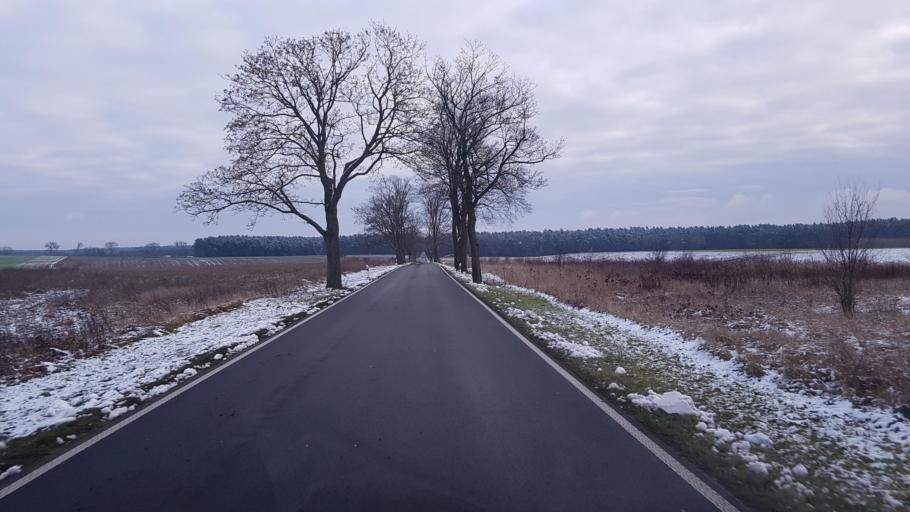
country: DE
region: Brandenburg
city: Strausberg
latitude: 52.5637
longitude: 13.9025
